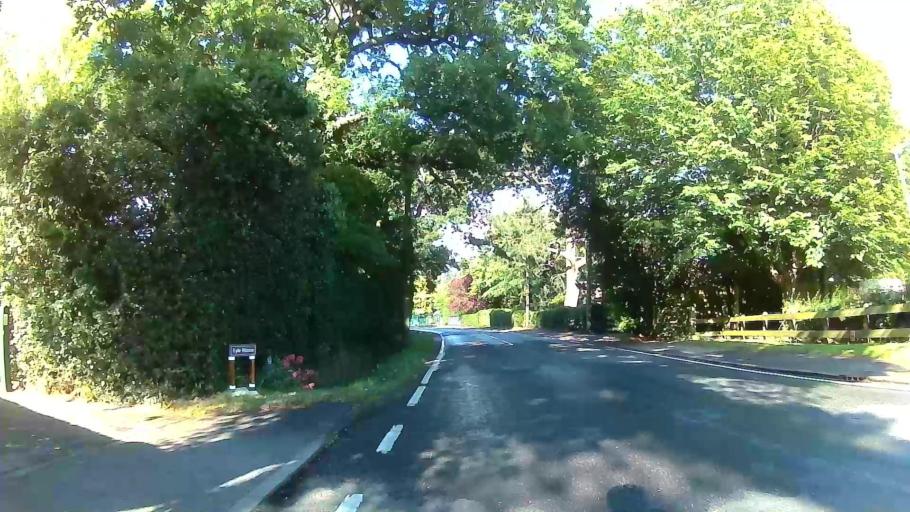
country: GB
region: England
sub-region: Essex
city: Ingatestone
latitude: 51.7103
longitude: 0.3726
